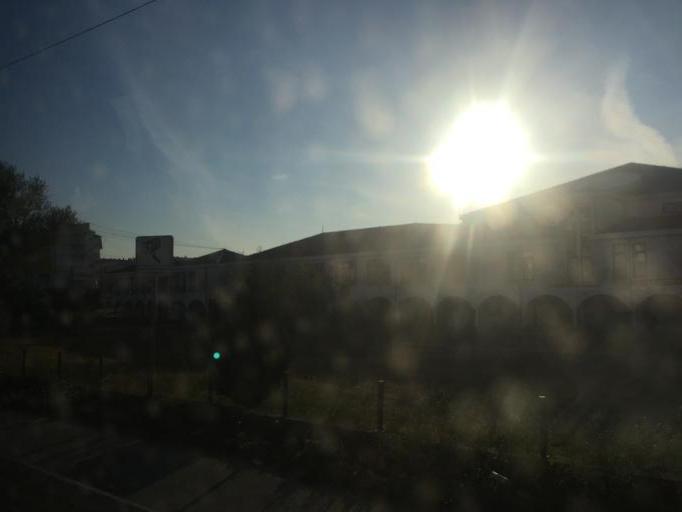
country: XK
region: Pristina
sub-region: Komuna e Drenasit
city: Glogovac
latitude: 42.6213
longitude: 20.8908
